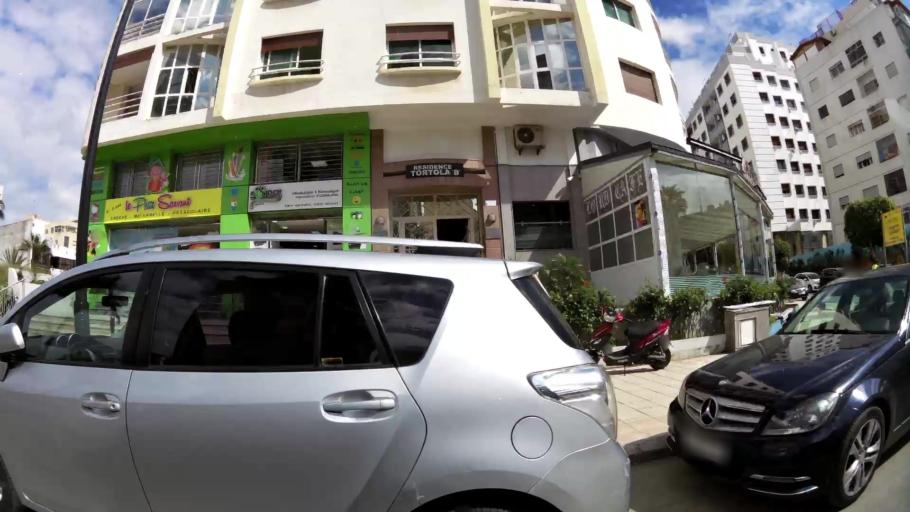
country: MA
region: Tanger-Tetouan
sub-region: Tanger-Assilah
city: Tangier
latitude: 35.7732
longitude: -5.8075
